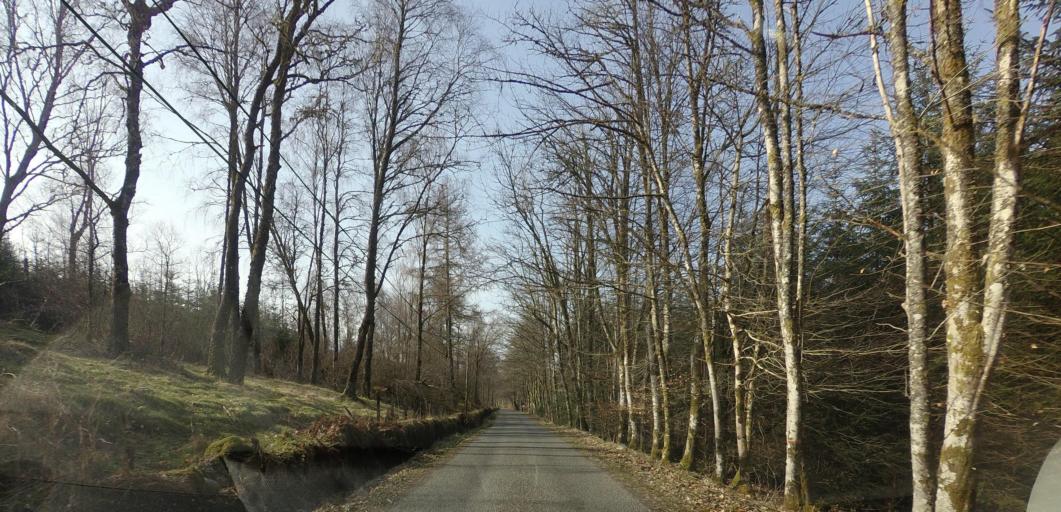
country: GB
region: Scotland
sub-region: Stirling
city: Callander
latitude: 56.4647
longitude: -4.2922
